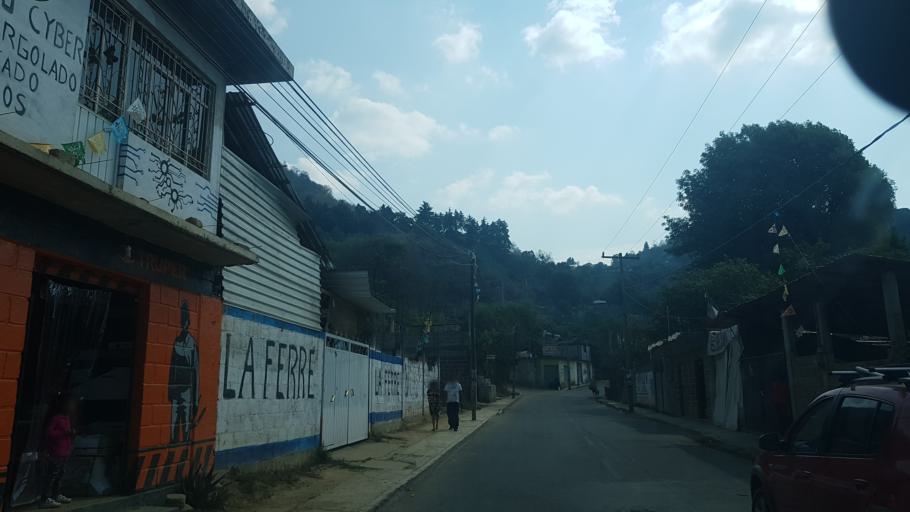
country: MX
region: Puebla
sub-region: Tochimilco
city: San Antonio Alpanocan
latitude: 18.8774
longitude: -98.7067
